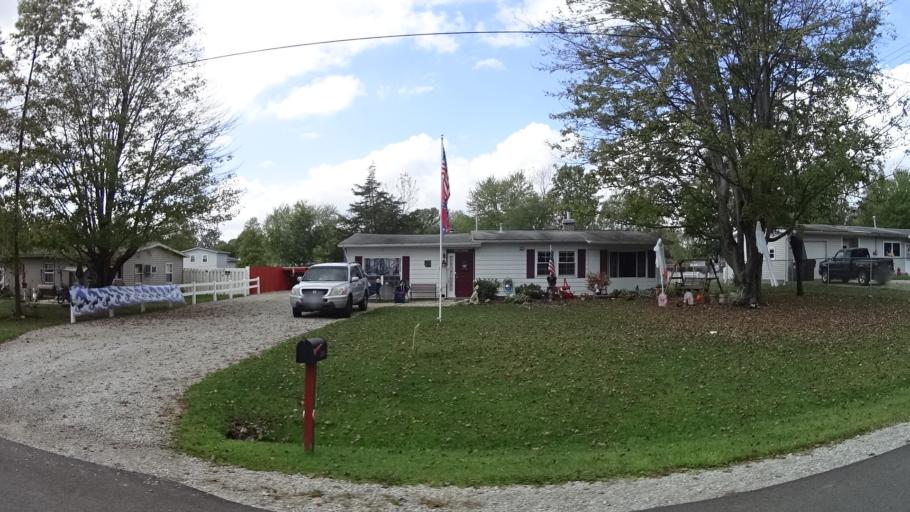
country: US
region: Ohio
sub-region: Lorain County
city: Eaton Estates
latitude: 41.3084
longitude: -82.0042
